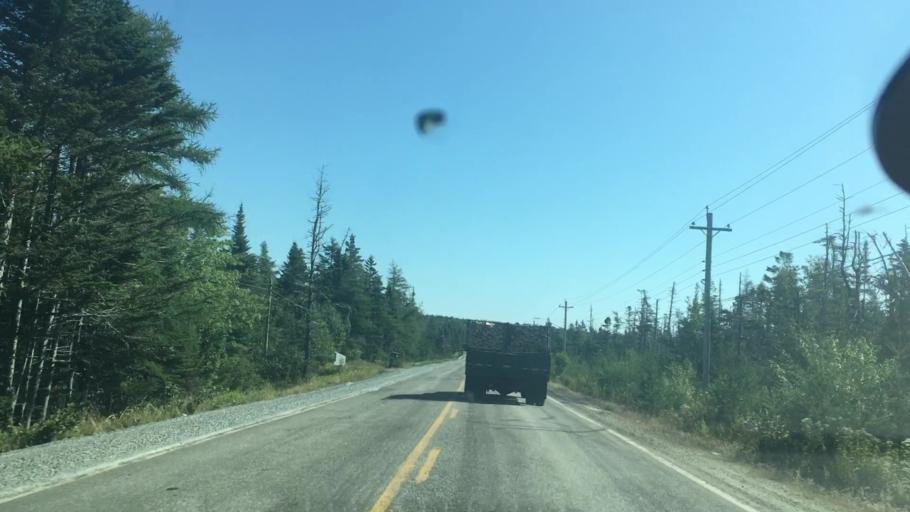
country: CA
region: Nova Scotia
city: New Glasgow
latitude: 44.9034
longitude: -62.4571
